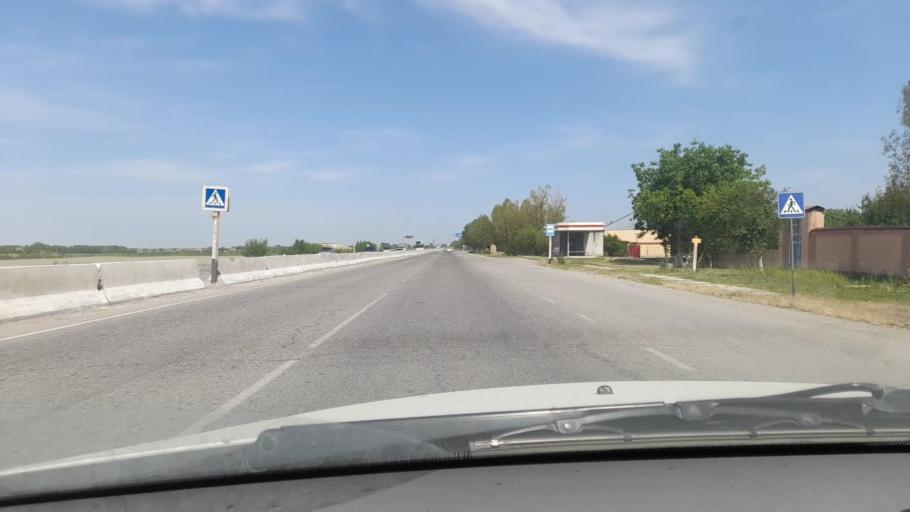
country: UZ
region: Samarqand
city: Kattaqo'rg'on
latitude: 39.9175
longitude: 66.3293
